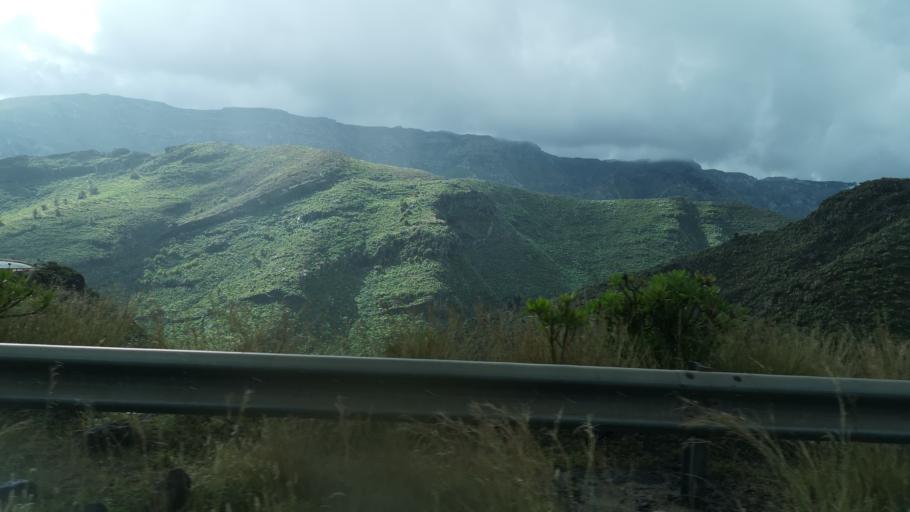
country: ES
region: Canary Islands
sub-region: Provincia de Santa Cruz de Tenerife
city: San Sebastian de la Gomera
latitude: 28.1234
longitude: -17.1459
